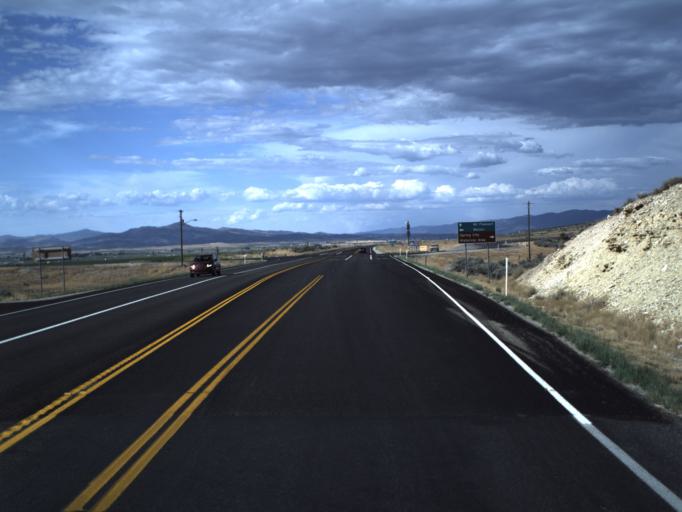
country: US
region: Utah
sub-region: Sanpete County
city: Ephraim
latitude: 39.4202
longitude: -111.5594
